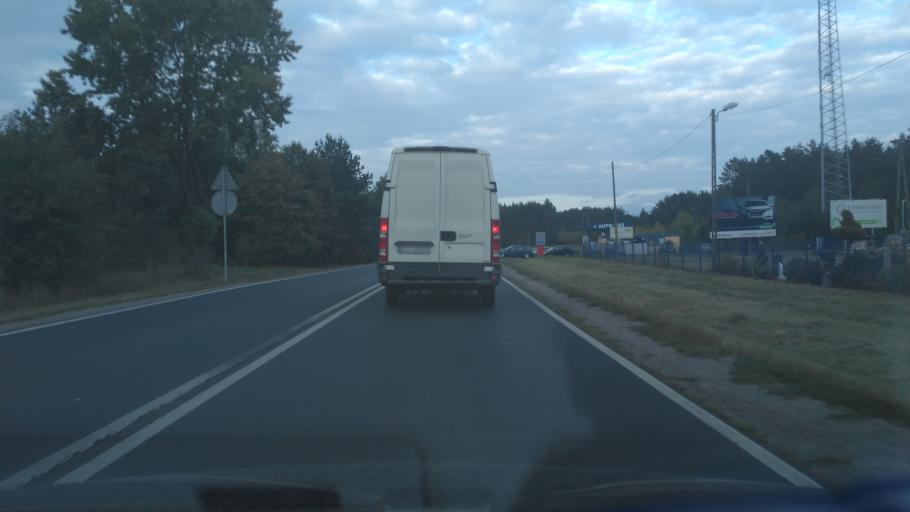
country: PL
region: Lublin Voivodeship
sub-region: Powiat lubelski
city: Jakubowice Murowane
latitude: 51.2909
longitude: 22.7022
